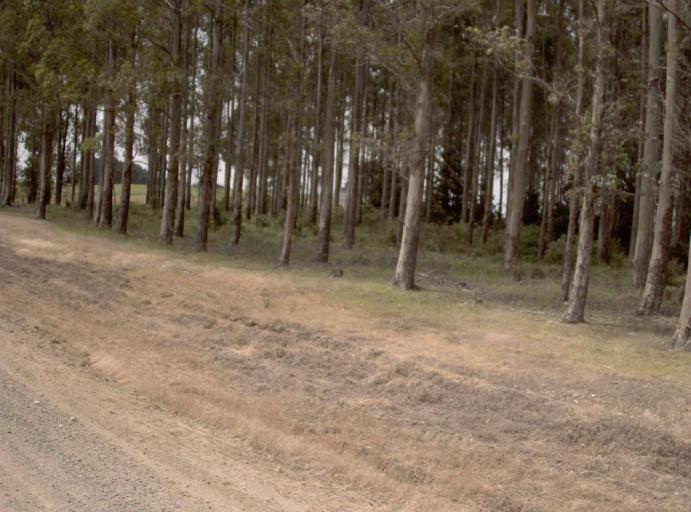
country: AU
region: Victoria
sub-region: Latrobe
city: Traralgon
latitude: -38.3765
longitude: 146.6752
